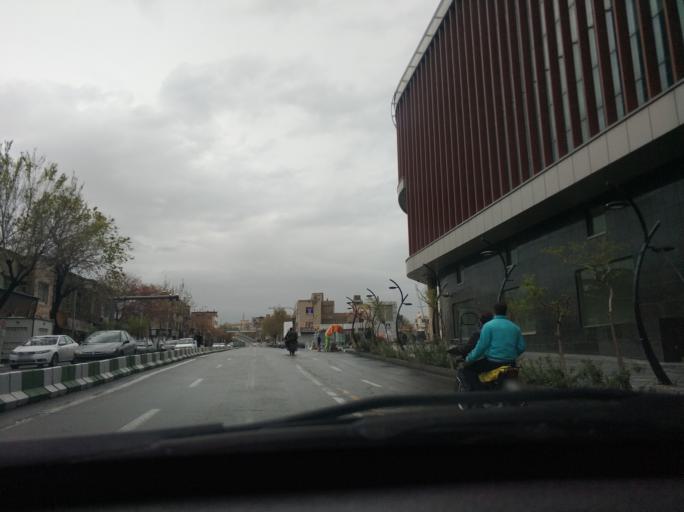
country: IR
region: Tehran
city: Tehran
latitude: 35.6983
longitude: 51.4367
